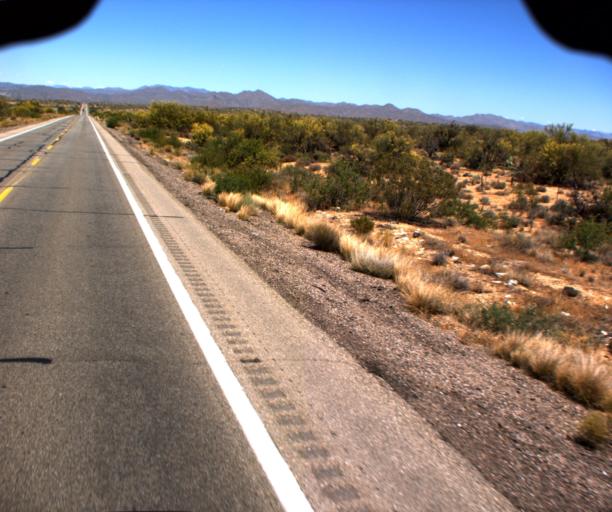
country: US
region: Arizona
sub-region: Yavapai County
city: Bagdad
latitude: 34.3212
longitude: -113.1354
